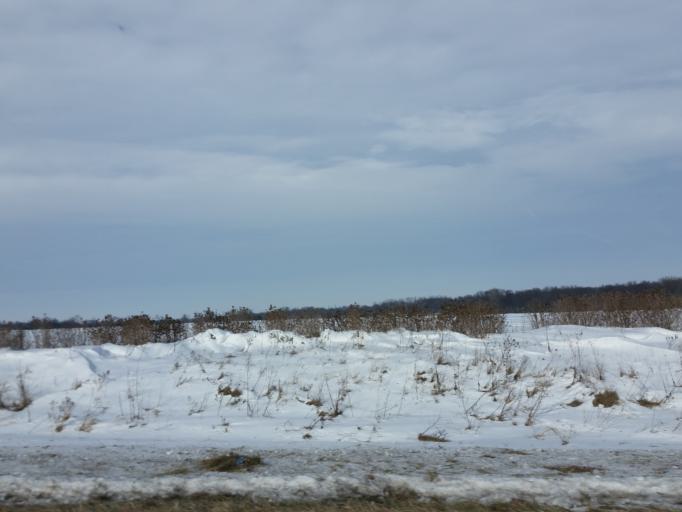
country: US
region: Iowa
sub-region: Buchanan County
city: Independence
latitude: 42.4612
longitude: -91.7188
